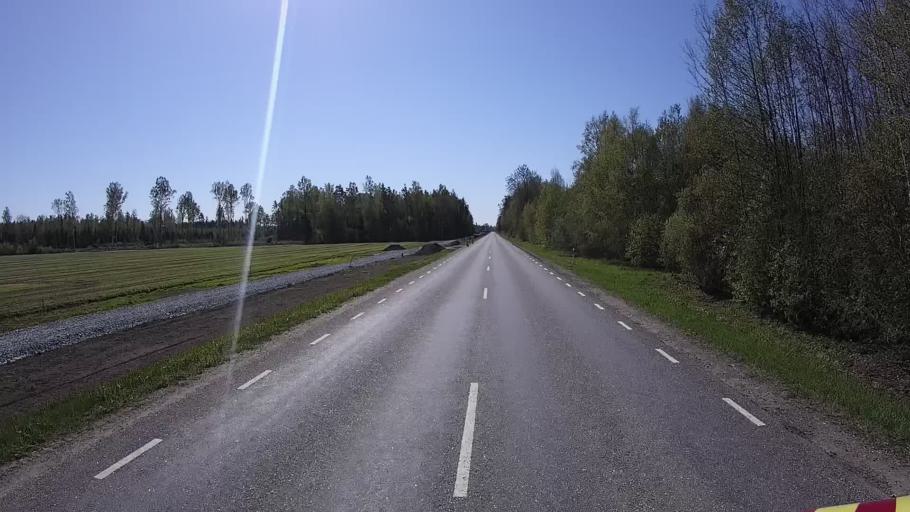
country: EE
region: Paernumaa
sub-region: Tootsi vald
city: Tootsi
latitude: 58.5002
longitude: 24.8002
